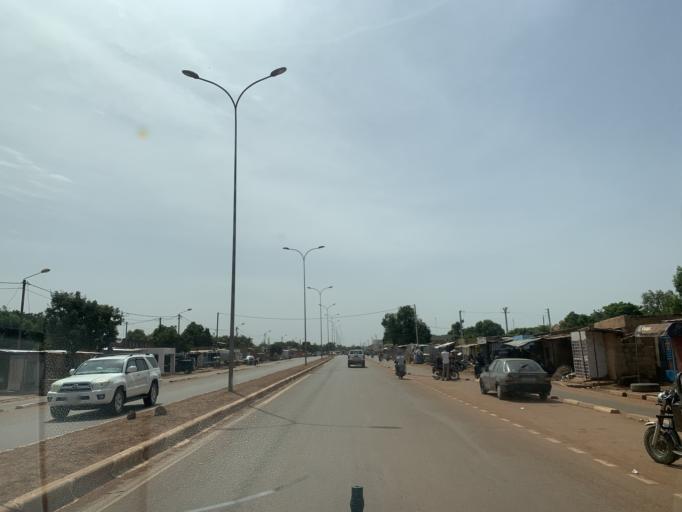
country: BF
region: Centre
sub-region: Kadiogo Province
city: Ouagadougou
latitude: 12.3394
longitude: -1.5158
